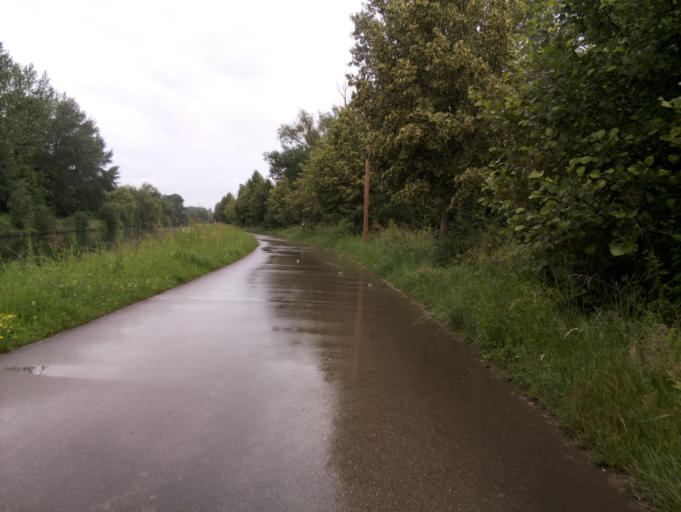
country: FR
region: Picardie
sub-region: Departement de la Somme
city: Ailly-sur-Somme
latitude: 49.9327
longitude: 2.1899
